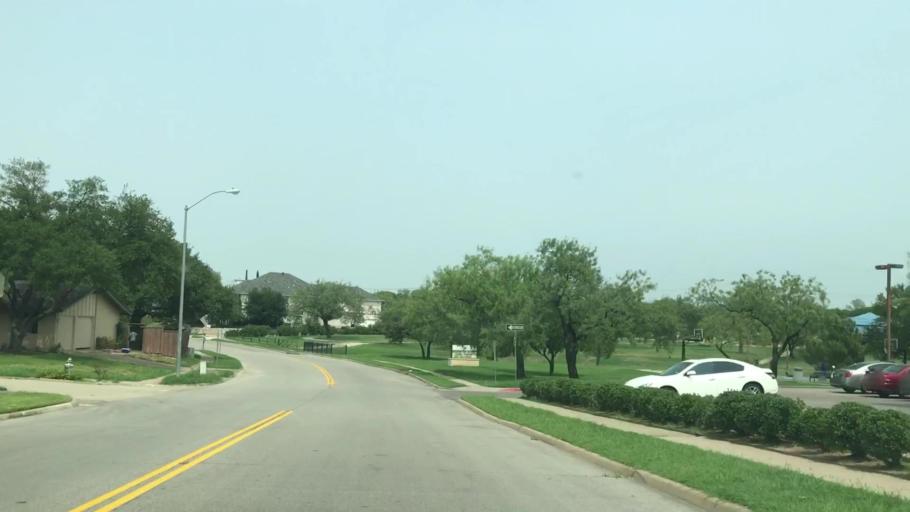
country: US
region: Texas
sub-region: Dallas County
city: Irving
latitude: 32.8442
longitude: -97.0023
